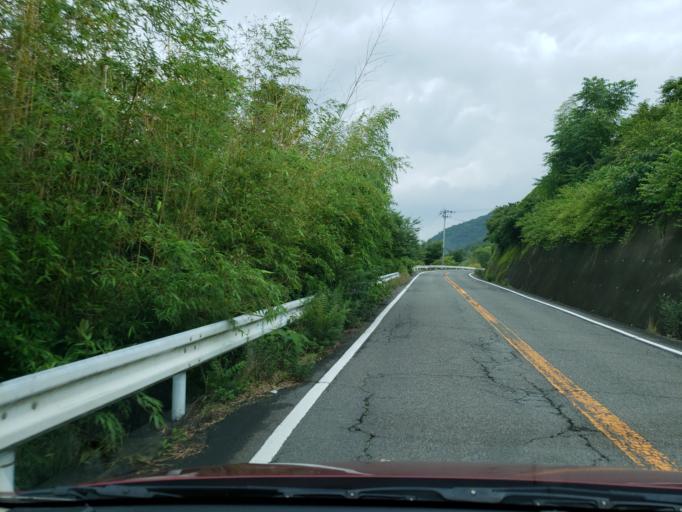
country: JP
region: Tokushima
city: Kamojimacho-jogejima
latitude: 34.1069
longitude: 134.2793
